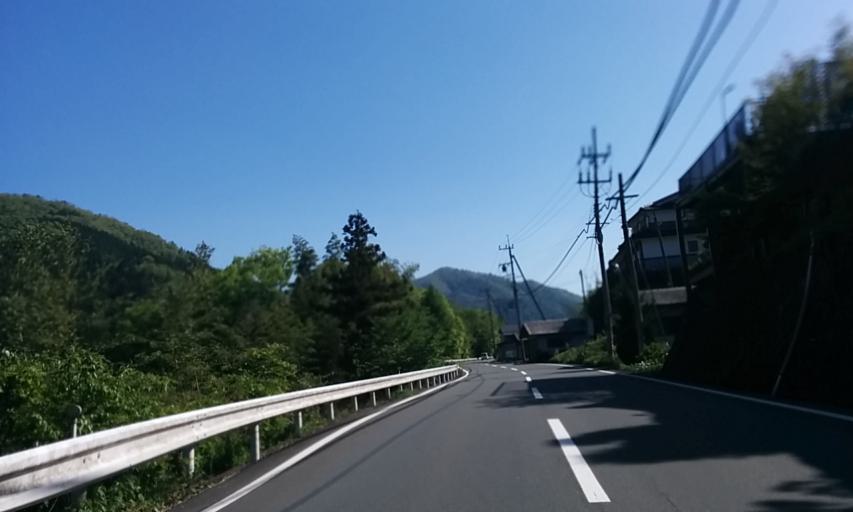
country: JP
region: Kyoto
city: Ayabe
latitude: 35.2621
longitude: 135.4293
